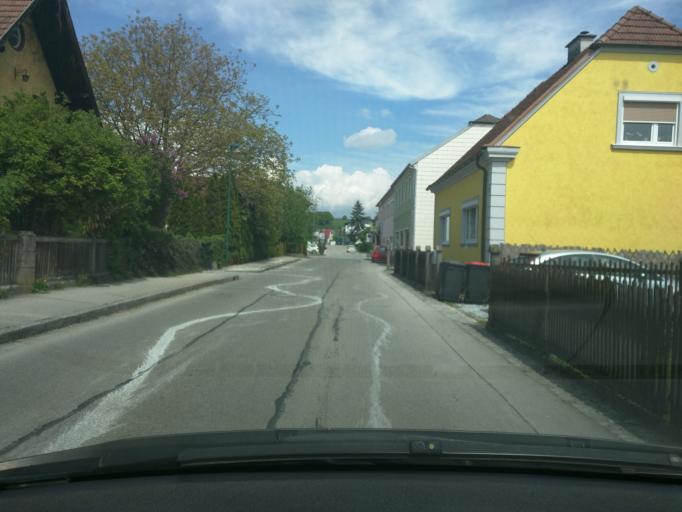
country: AT
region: Lower Austria
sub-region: Politischer Bezirk Melk
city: Blindenmarkt
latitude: 48.1277
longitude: 14.9870
